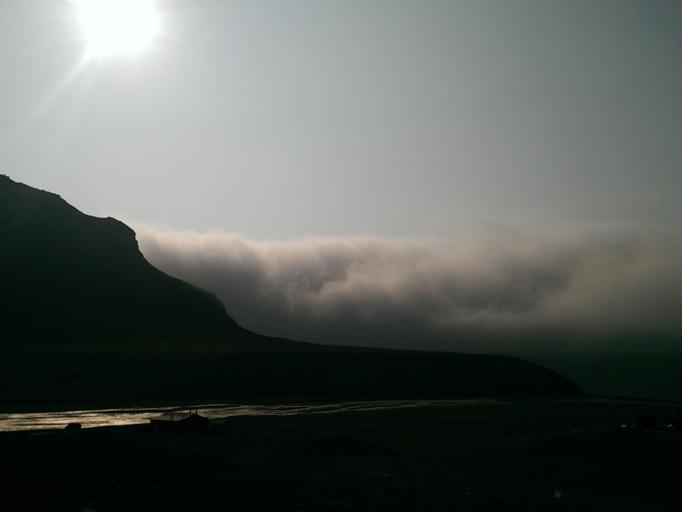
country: SJ
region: Svalbard
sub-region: Spitsbergen
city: Longyearbyen
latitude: 78.2254
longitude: 15.3283
